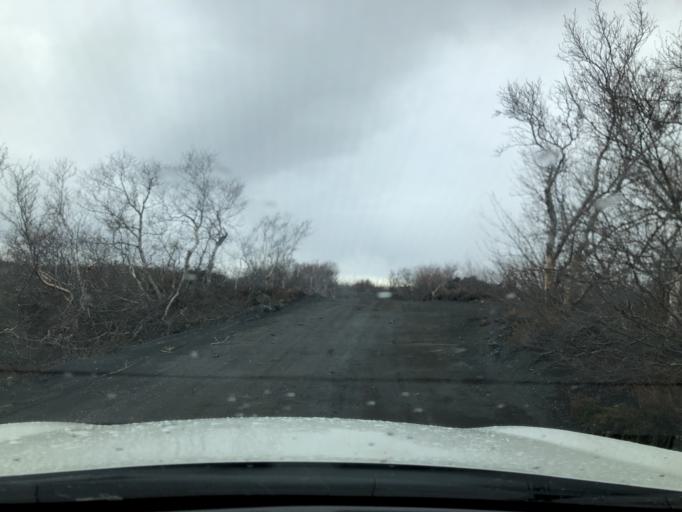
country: IS
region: Northeast
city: Laugar
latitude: 65.6074
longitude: -16.8975
